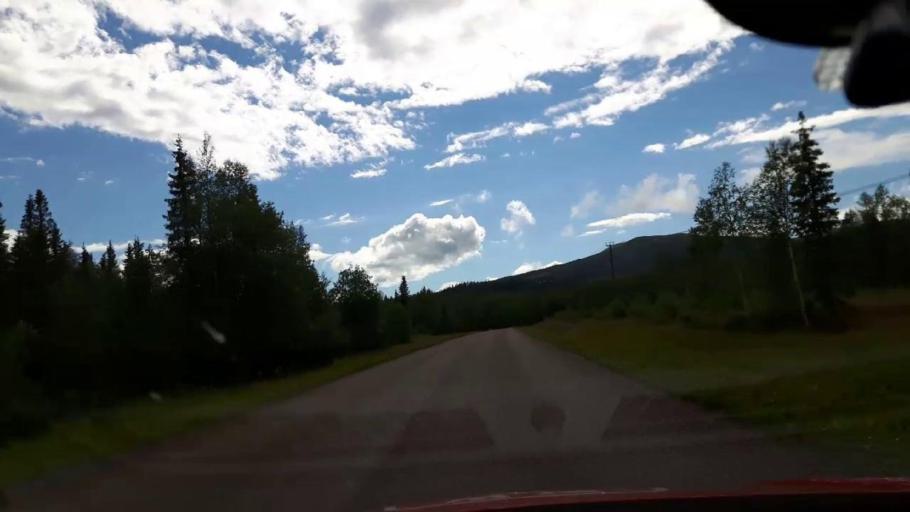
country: SE
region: Jaemtland
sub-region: Are Kommun
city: Are
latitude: 63.3060
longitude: 13.2250
